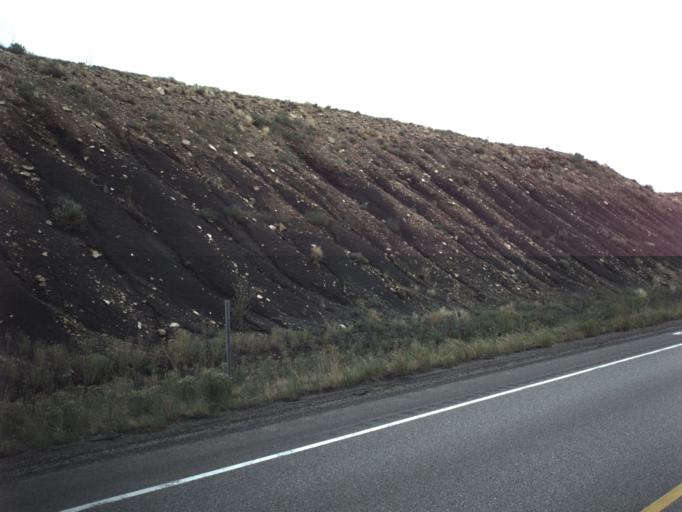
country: US
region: Utah
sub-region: Carbon County
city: East Carbon City
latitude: 39.5162
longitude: -110.5513
